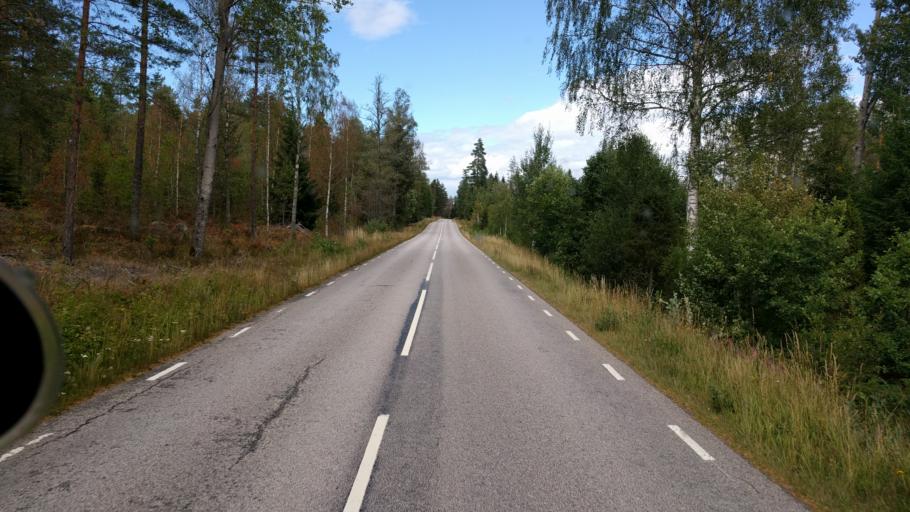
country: SE
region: Kalmar
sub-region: Vasterviks Kommun
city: Ankarsrum
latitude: 57.7631
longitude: 16.1357
